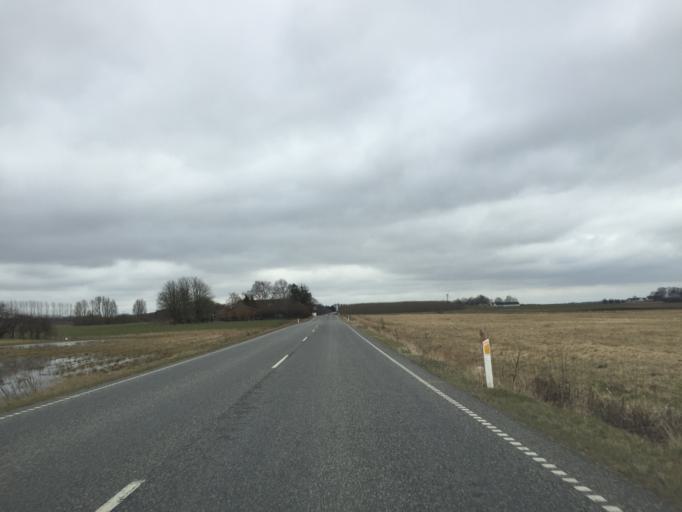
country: DK
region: Capital Region
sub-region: Allerod Kommune
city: Lynge
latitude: 55.8776
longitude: 12.2730
